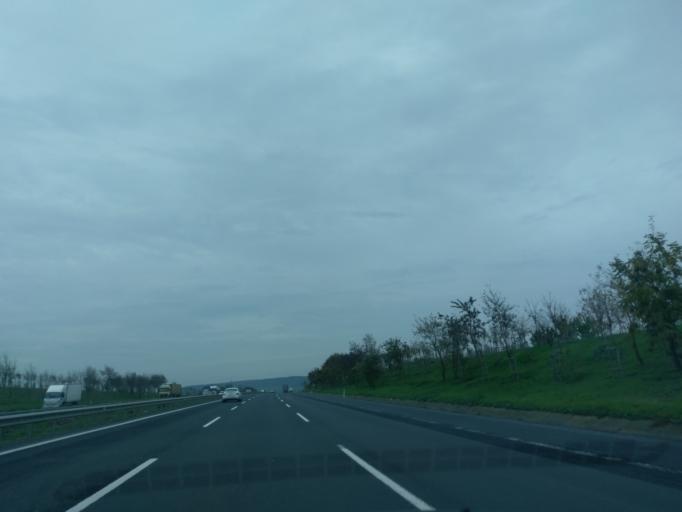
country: TR
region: Istanbul
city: Canta
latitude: 41.1424
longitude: 28.1488
